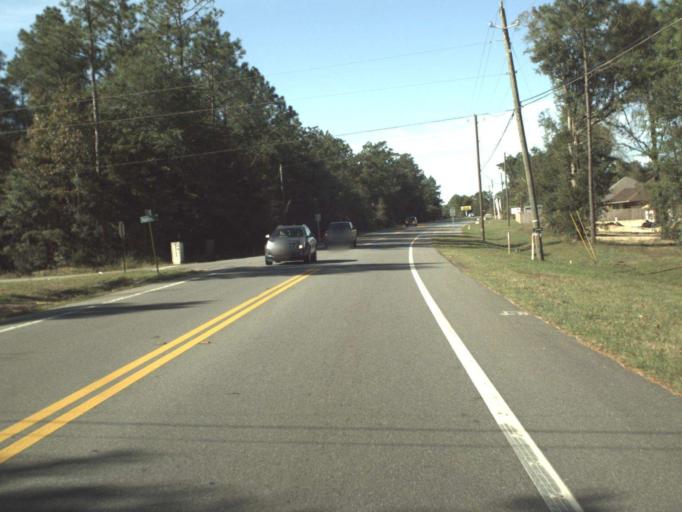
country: US
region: Florida
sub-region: Okaloosa County
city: Crestview
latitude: 30.7634
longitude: -86.6651
